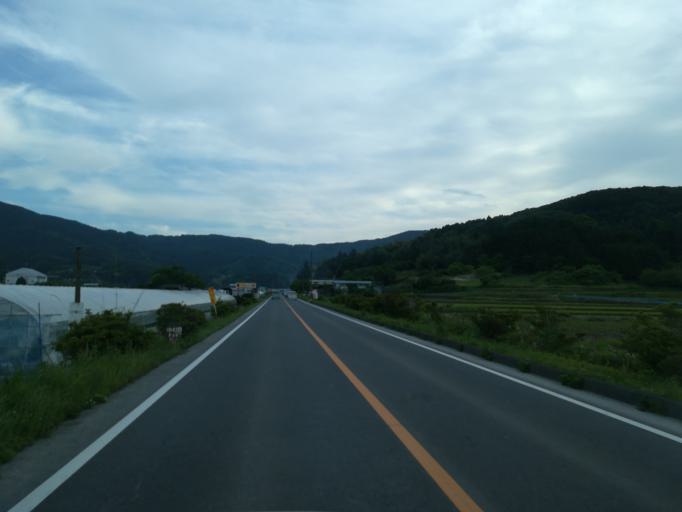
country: JP
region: Ibaraki
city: Tsukuba
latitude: 36.1945
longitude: 140.1751
